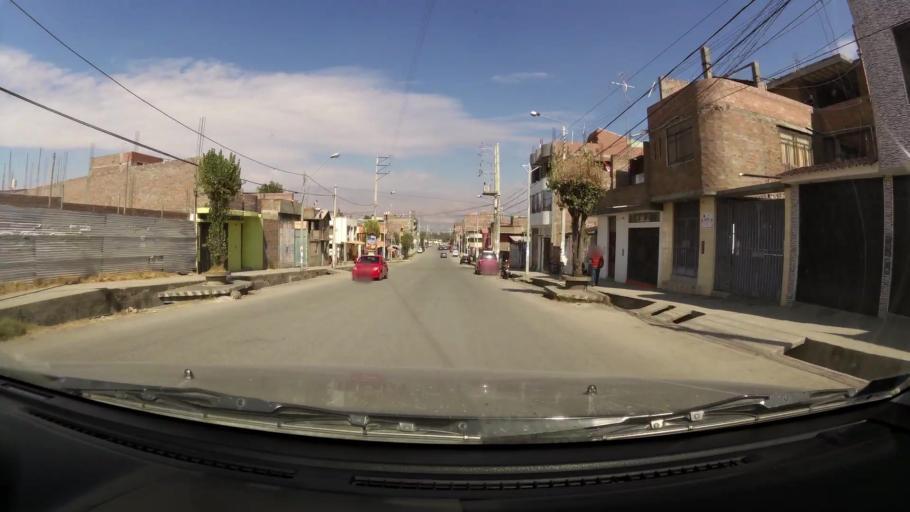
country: PE
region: Junin
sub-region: Provincia de Huancayo
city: El Tambo
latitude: -12.0772
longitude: -75.2279
